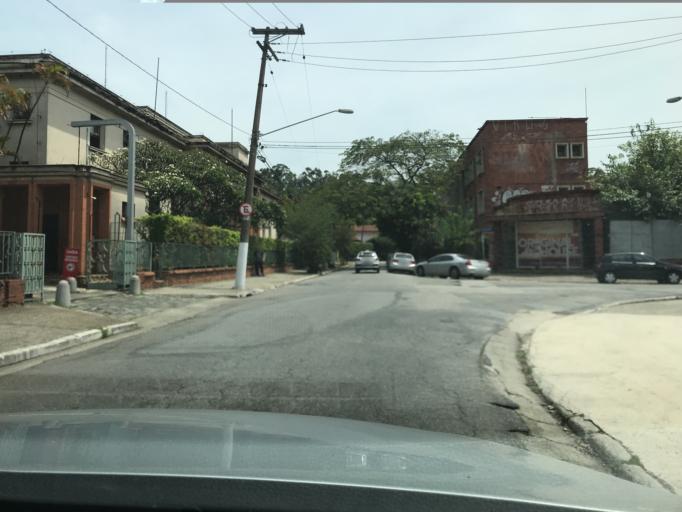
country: BR
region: Sao Paulo
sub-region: Sao Paulo
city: Sao Paulo
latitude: -23.5738
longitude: -46.7011
